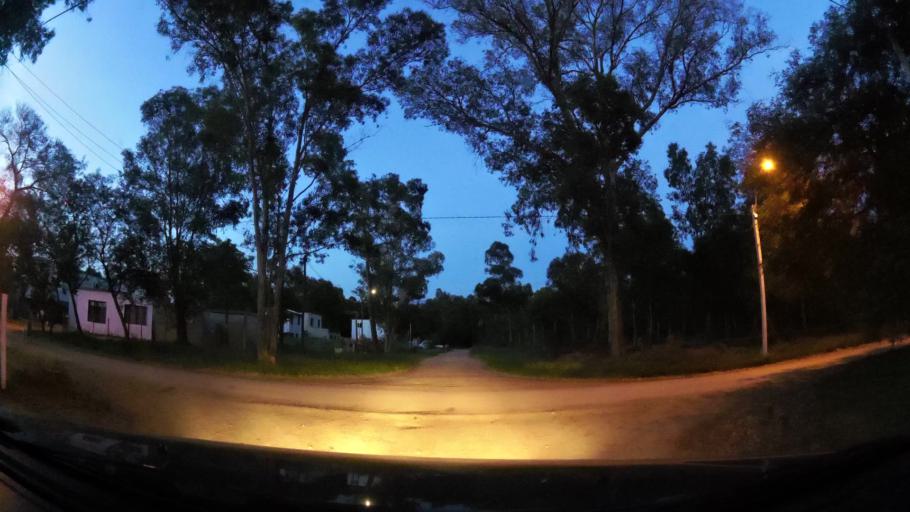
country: UY
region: Canelones
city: Atlantida
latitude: -34.7630
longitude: -55.7556
